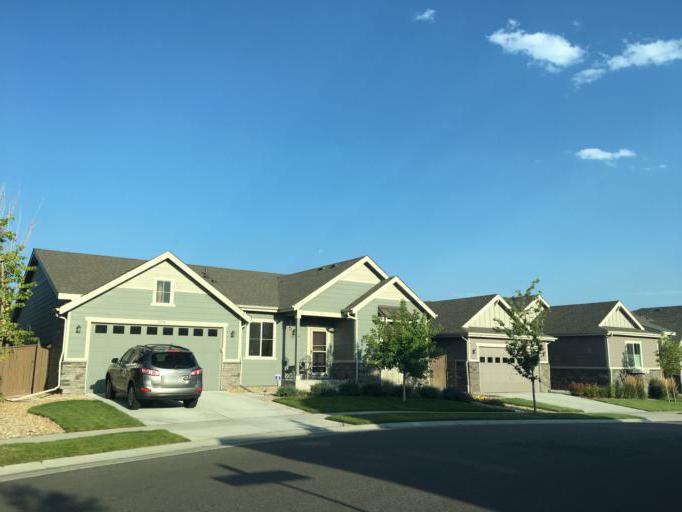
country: US
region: Colorado
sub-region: Jefferson County
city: Applewood
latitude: 39.7890
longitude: -105.1705
